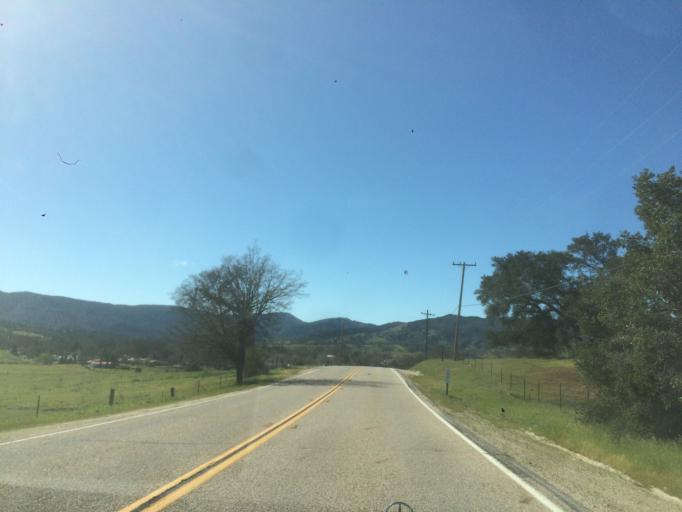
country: US
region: California
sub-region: San Luis Obispo County
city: Santa Margarita
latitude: 35.3914
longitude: -120.5949
